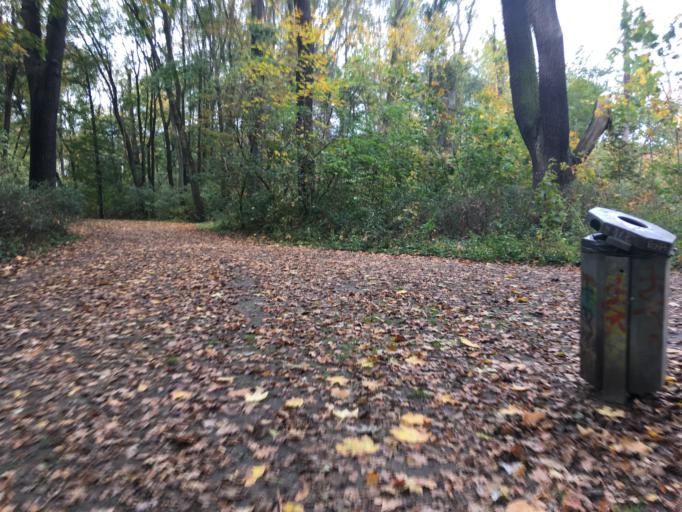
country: DE
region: Berlin
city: Plaenterwald
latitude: 52.4850
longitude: 13.4760
